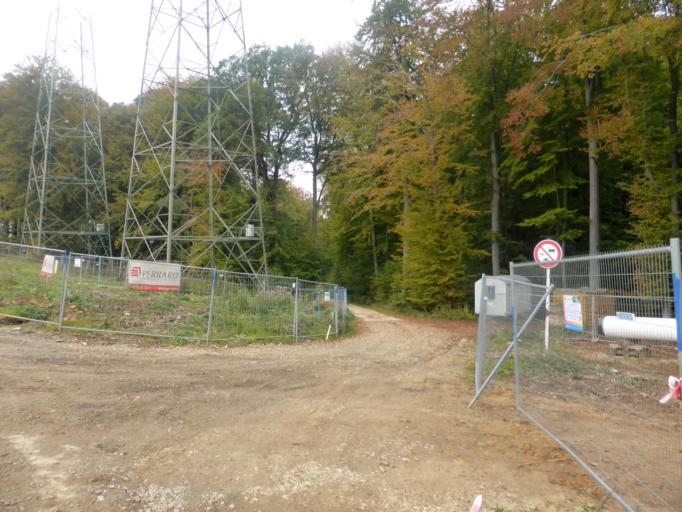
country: LU
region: Luxembourg
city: Kirchberg
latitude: 49.6381
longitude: 6.1808
